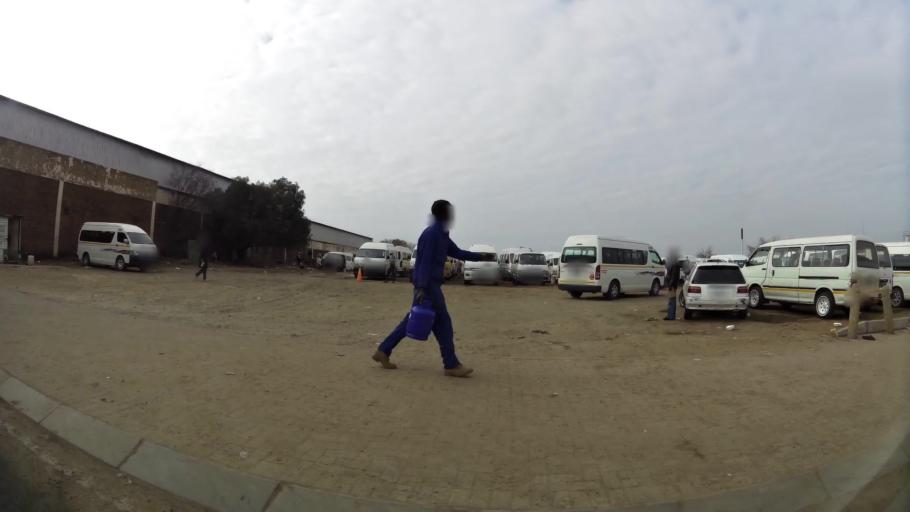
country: ZA
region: Orange Free State
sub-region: Mangaung Metropolitan Municipality
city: Bloemfontein
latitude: -29.1285
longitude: 26.2232
